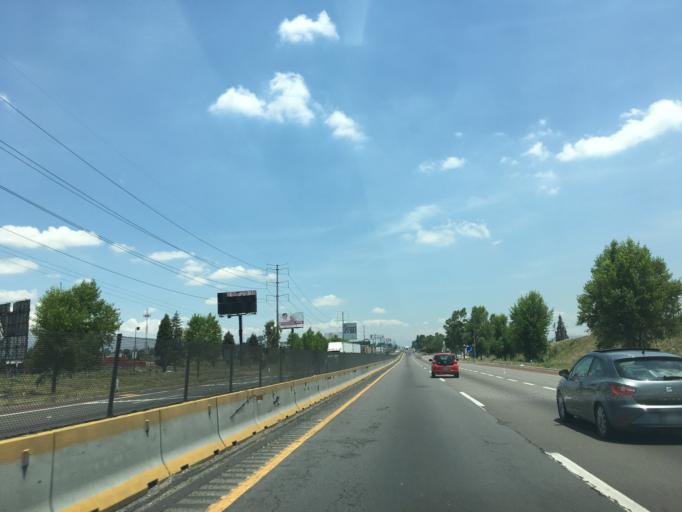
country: MX
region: Puebla
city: Ocotlan
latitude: 19.1358
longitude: -98.2723
